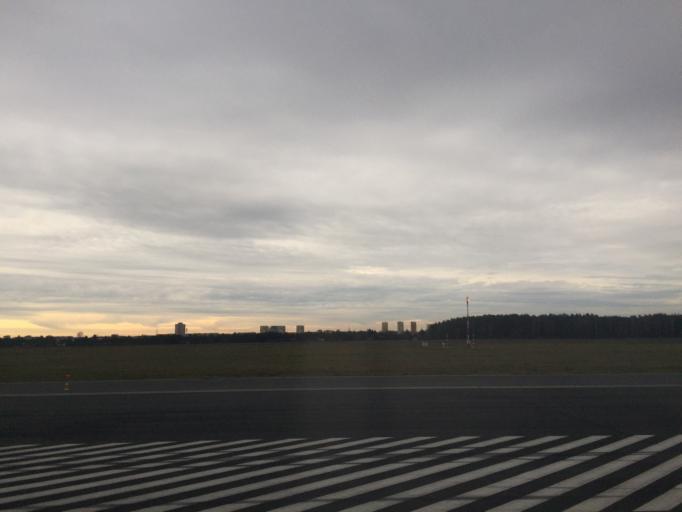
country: PL
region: Kujawsko-Pomorskie
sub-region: Bydgoszcz
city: Bydgoszcz
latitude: 53.0981
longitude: 17.9910
